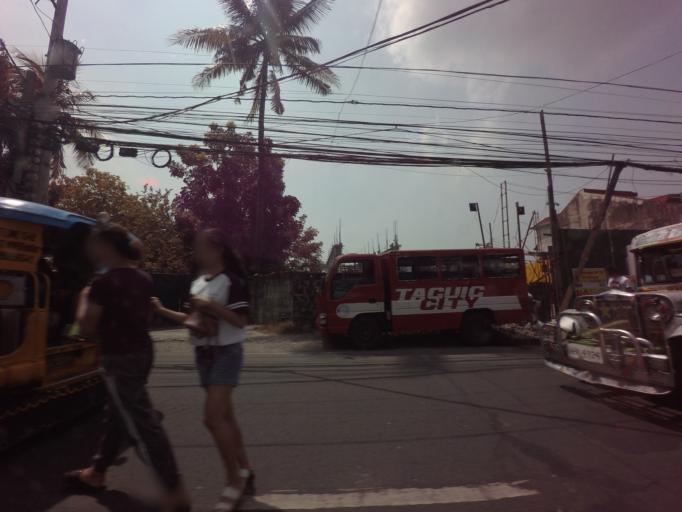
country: PH
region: Calabarzon
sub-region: Province of Rizal
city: Taguig
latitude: 14.4990
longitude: 121.0633
